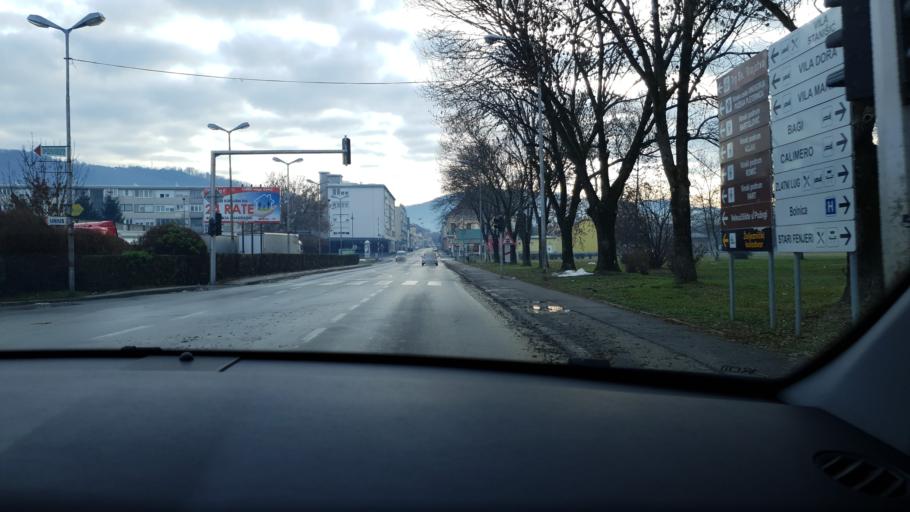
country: HR
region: Pozesko-Slavonska
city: Pozega
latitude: 45.3388
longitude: 17.6812
